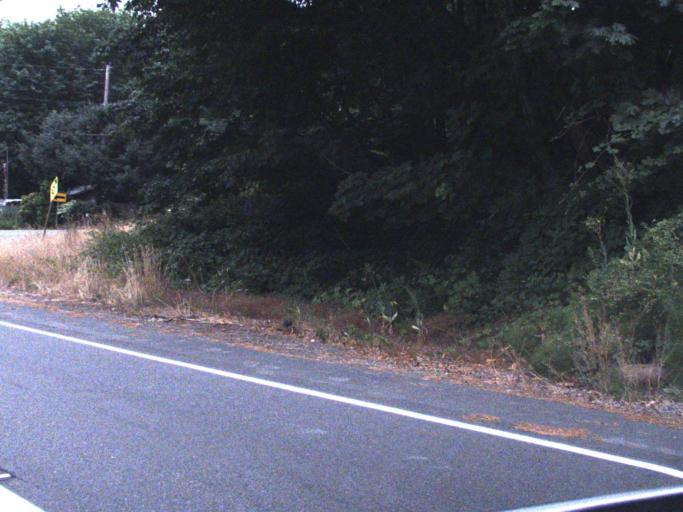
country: US
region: Washington
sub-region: King County
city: Lake Marcel-Stillwater
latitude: 47.6827
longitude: -121.9196
